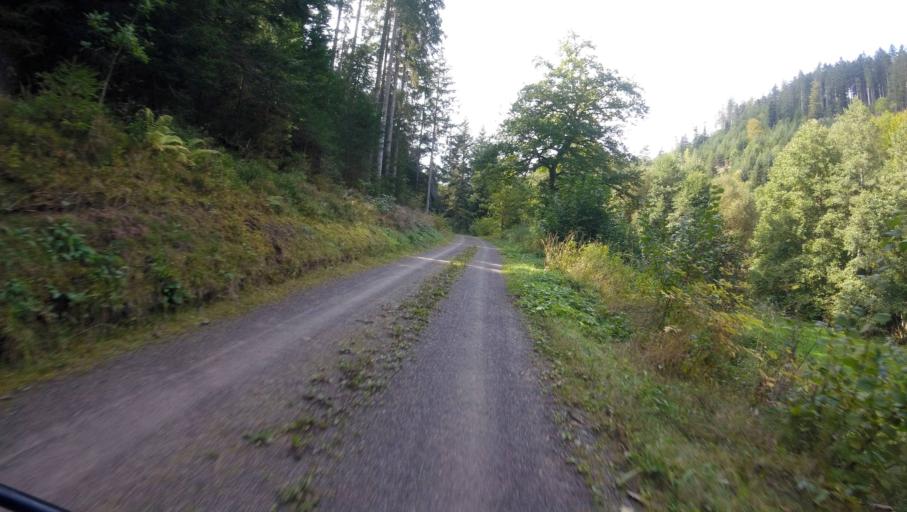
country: DE
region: Baden-Wuerttemberg
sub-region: Karlsruhe Region
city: Grombach
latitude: 48.5893
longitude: 8.5581
